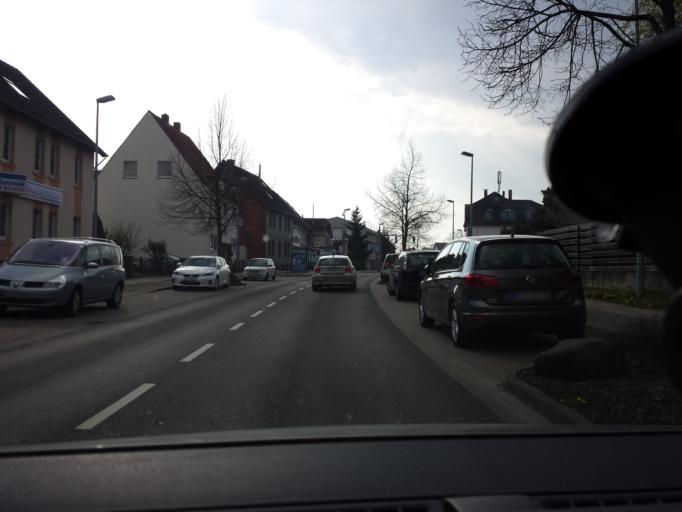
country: DE
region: Lower Saxony
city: Braunschweig
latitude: 52.2719
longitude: 10.4881
